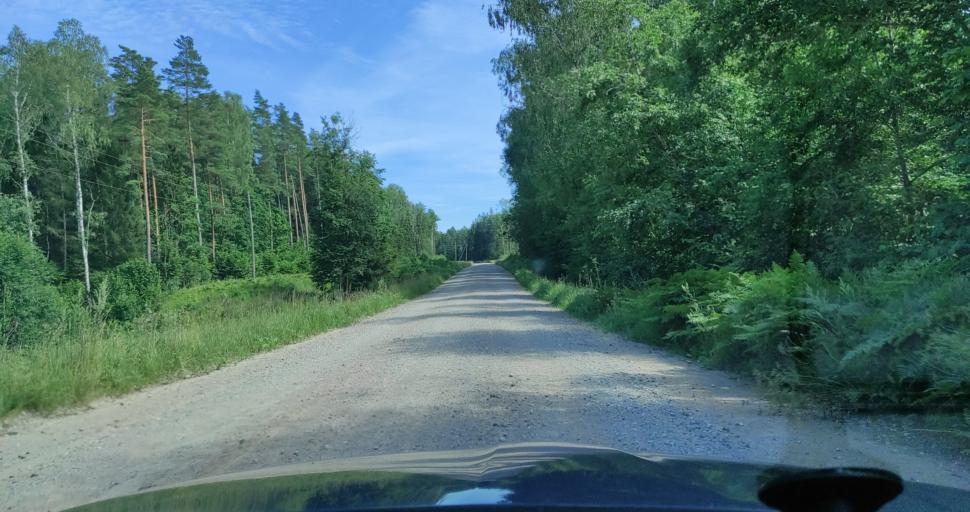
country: LV
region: Durbe
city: Liegi
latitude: 56.7559
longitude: 21.3353
